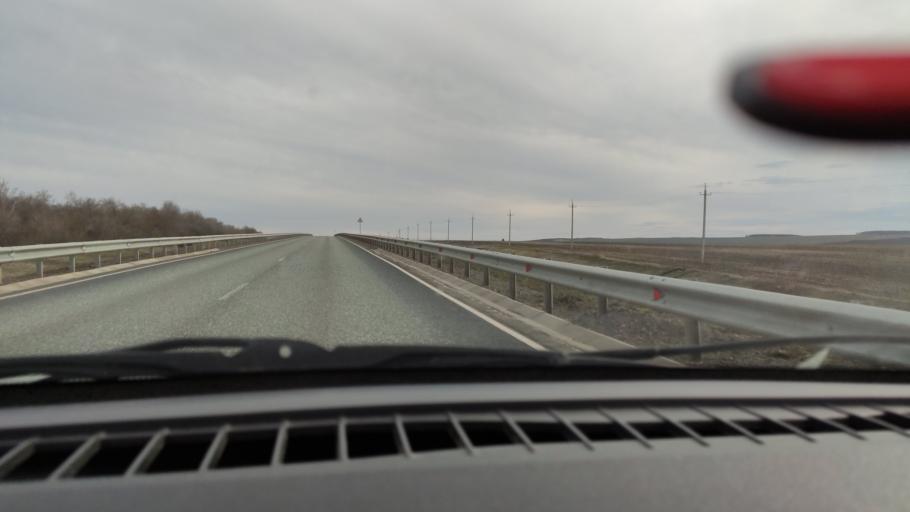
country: RU
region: Bashkortostan
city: Yermolayevo
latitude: 52.5485
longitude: 55.8368
